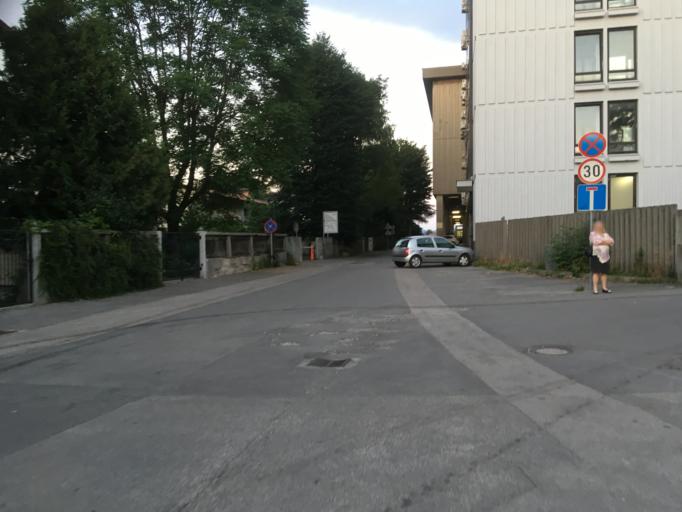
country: SI
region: Ljubljana
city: Ljubljana
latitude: 46.0601
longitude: 14.5040
